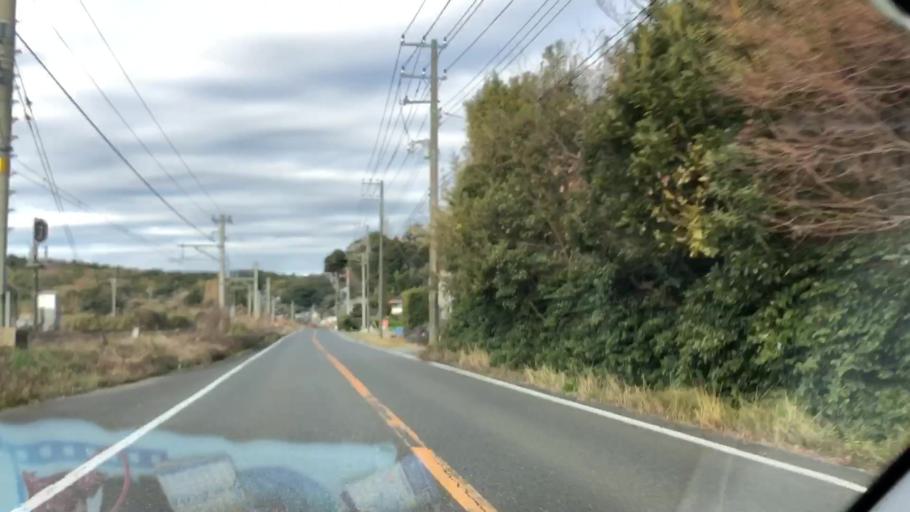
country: JP
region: Chiba
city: Tateyama
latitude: 34.9907
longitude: 139.9243
